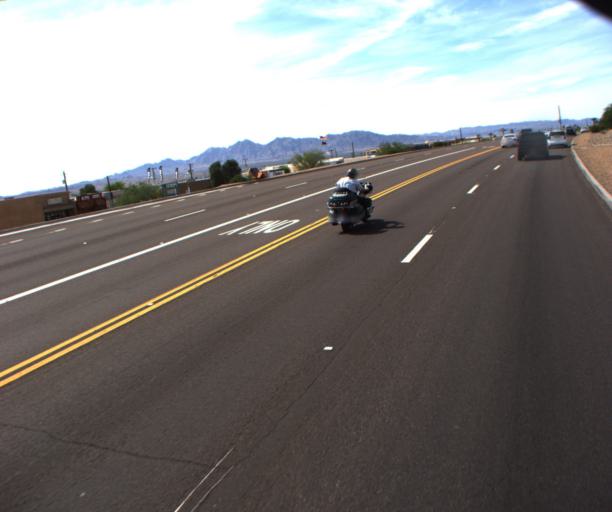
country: US
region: Arizona
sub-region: Mohave County
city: Lake Havasu City
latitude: 34.4753
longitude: -114.3471
